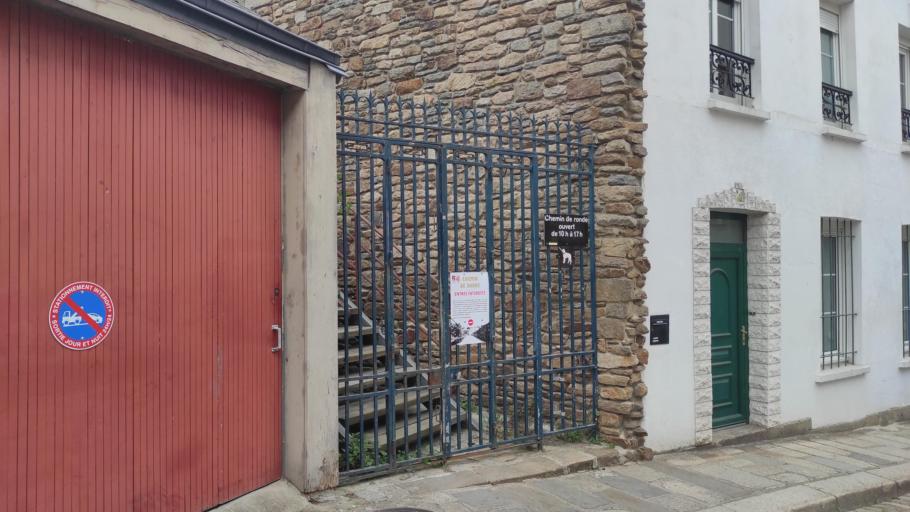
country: FR
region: Brittany
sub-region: Departement des Cotes-d'Armor
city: Dinan
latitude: 48.4549
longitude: -2.0410
